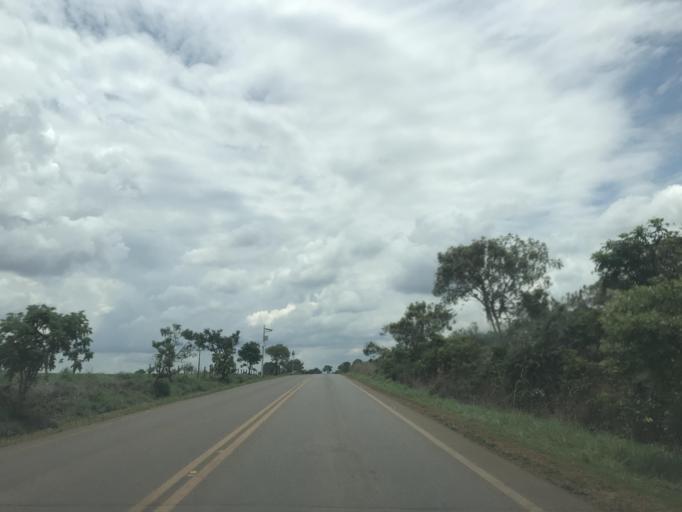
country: BR
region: Goias
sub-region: Vianopolis
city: Vianopolis
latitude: -16.7447
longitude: -48.4547
